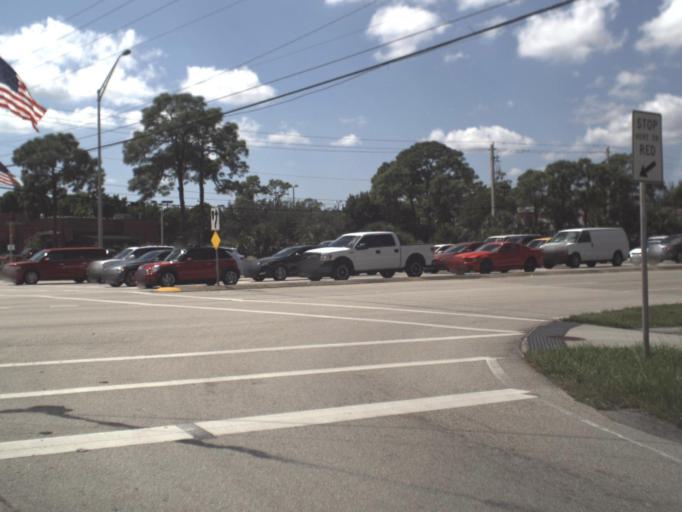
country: US
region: Florida
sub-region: Lee County
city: Villas
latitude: 26.5466
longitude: -81.8717
